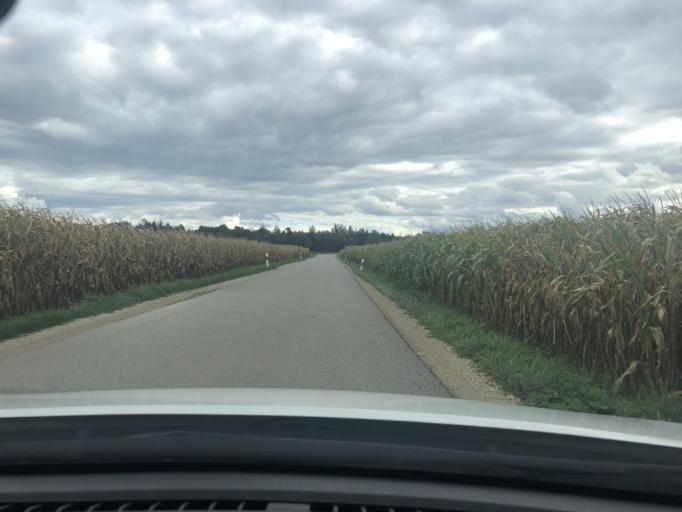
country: DE
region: Bavaria
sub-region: Upper Bavaria
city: Bergkirchen
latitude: 48.2373
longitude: 11.3364
